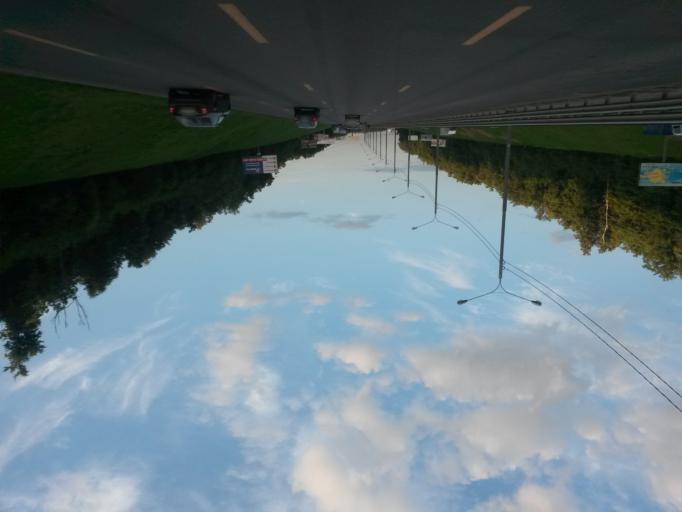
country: RU
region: Moscow
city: Annino
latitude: 55.5525
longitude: 37.6056
